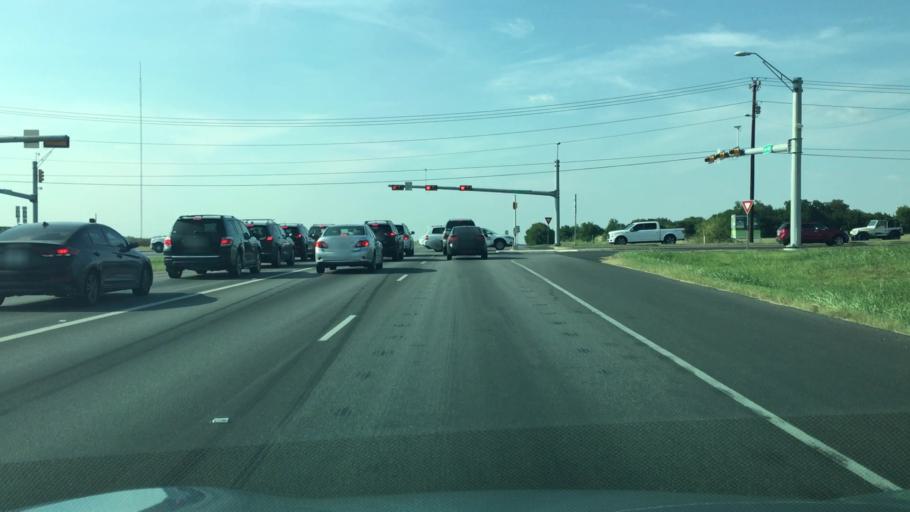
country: US
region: Texas
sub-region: Hays County
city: Kyle
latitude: 30.0276
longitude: -97.8725
